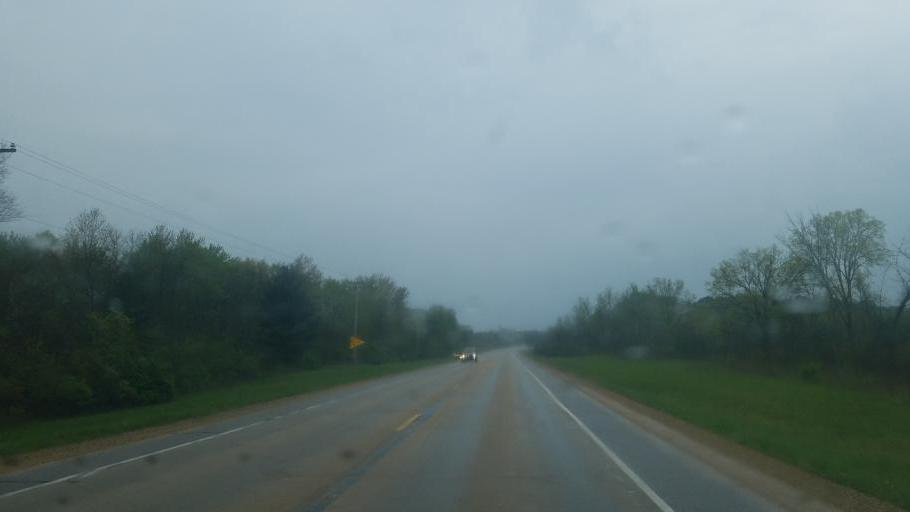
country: US
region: Wisconsin
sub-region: Juneau County
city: Elroy
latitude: 43.6242
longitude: -90.1649
